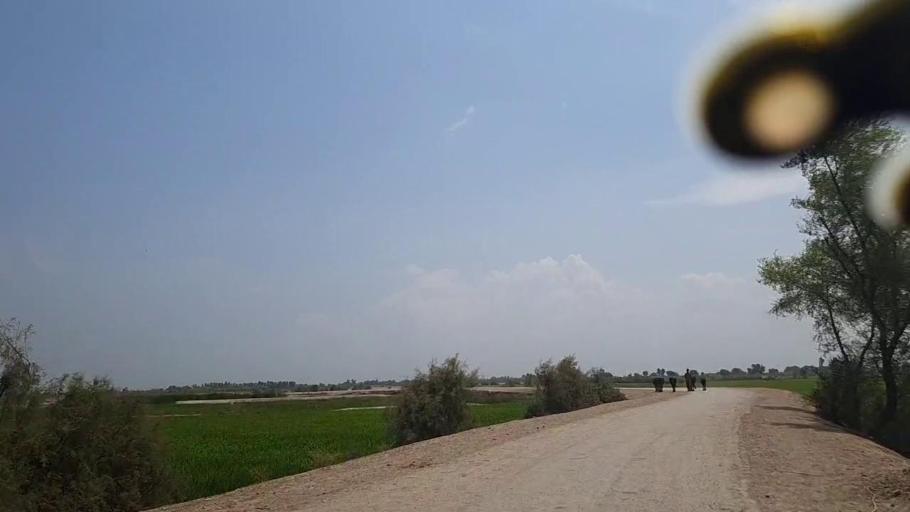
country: PK
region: Sindh
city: Rustam jo Goth
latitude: 28.1089
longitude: 68.8844
